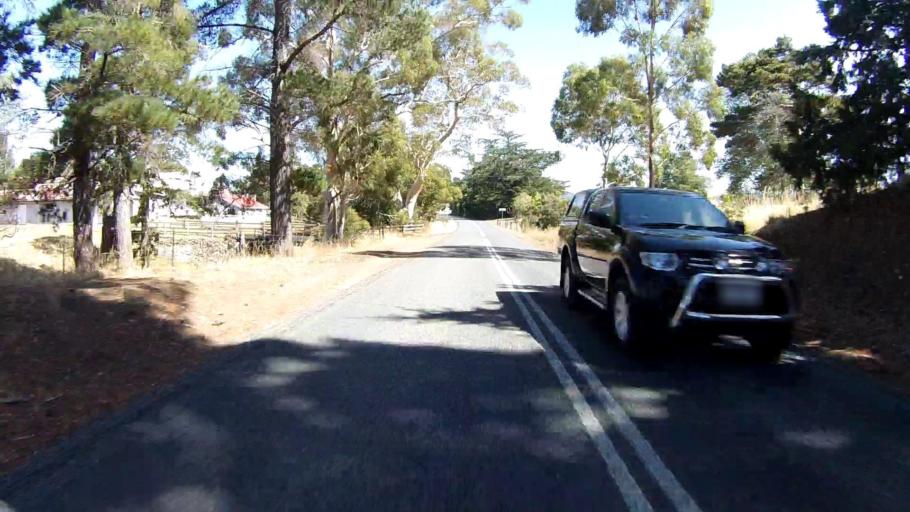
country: AU
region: Tasmania
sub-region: Sorell
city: Sorell
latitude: -42.4964
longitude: 147.9240
